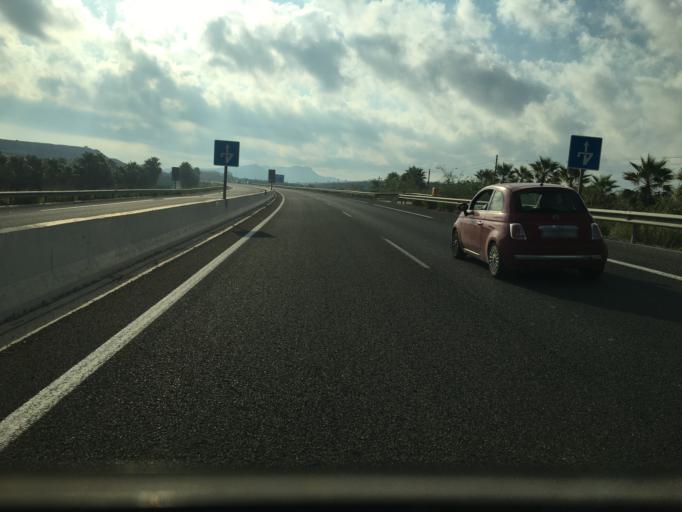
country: ES
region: Murcia
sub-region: Murcia
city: Beniel
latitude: 37.9951
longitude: -0.9993
